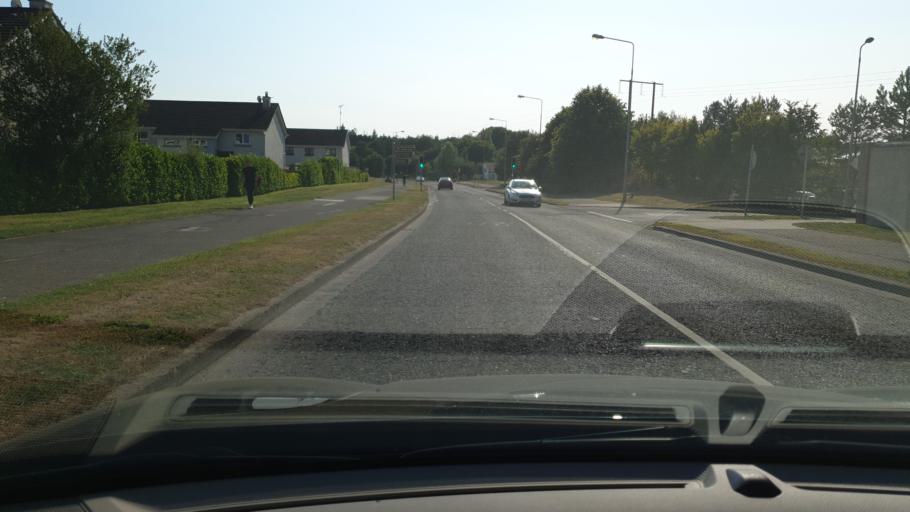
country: IE
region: Leinster
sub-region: An Mhi
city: Navan
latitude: 53.6663
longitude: -6.6933
